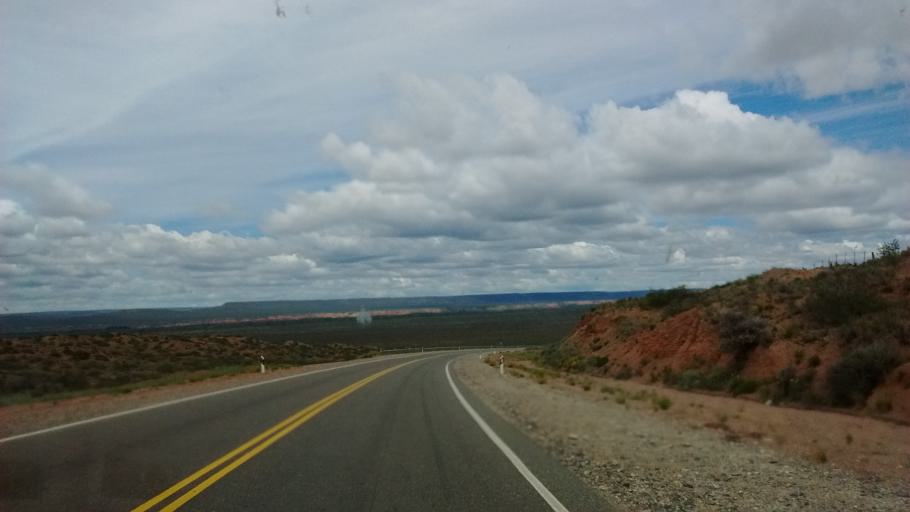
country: AR
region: Neuquen
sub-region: Departamento de Picun Leufu
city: Picun Leufu
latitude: -39.7781
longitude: -69.6543
